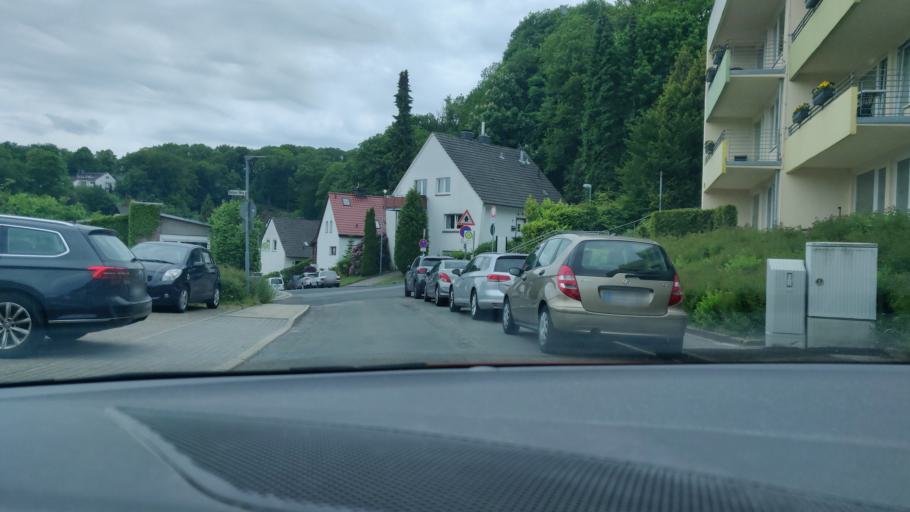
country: DE
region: North Rhine-Westphalia
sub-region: Regierungsbezirk Dusseldorf
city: Velbert
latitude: 51.3122
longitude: 7.0803
